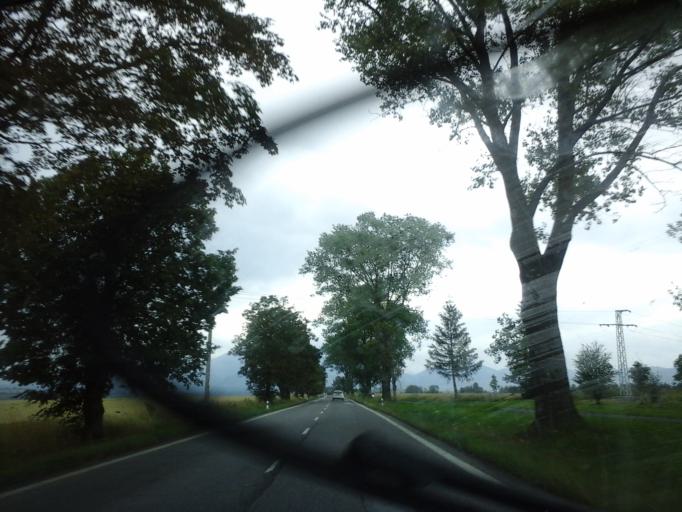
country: SK
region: Presovsky
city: Spisska Bela
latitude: 49.1962
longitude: 20.4350
